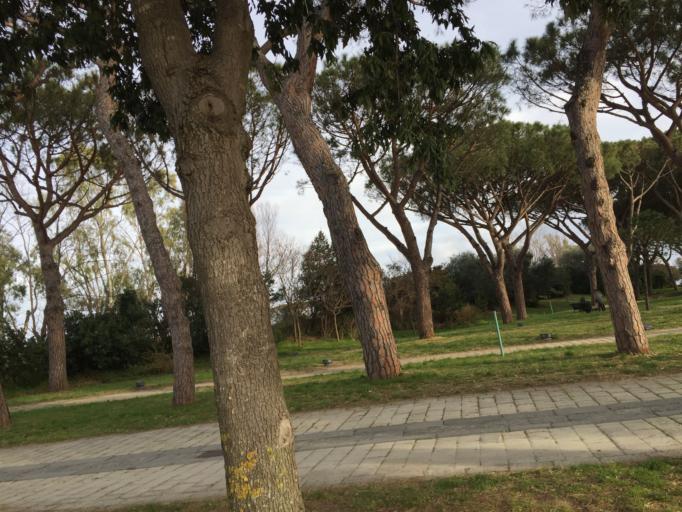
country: IT
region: Campania
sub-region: Provincia di Napoli
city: Bagnoli
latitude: 40.7989
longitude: 14.1772
